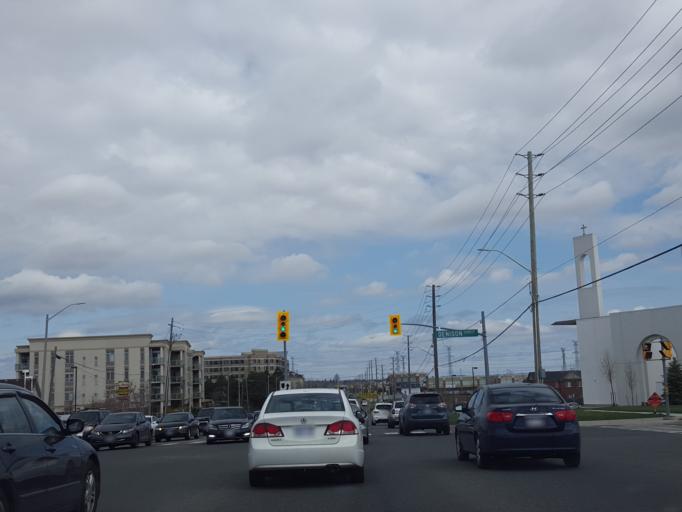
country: CA
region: Ontario
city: Markham
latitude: 43.8443
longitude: -79.2528
